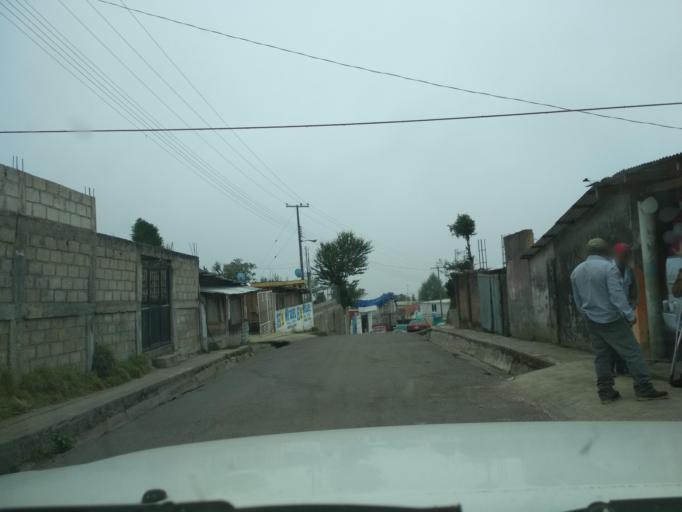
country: MX
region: Veracruz
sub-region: La Perla
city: Chilapa
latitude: 18.9760
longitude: -97.1904
